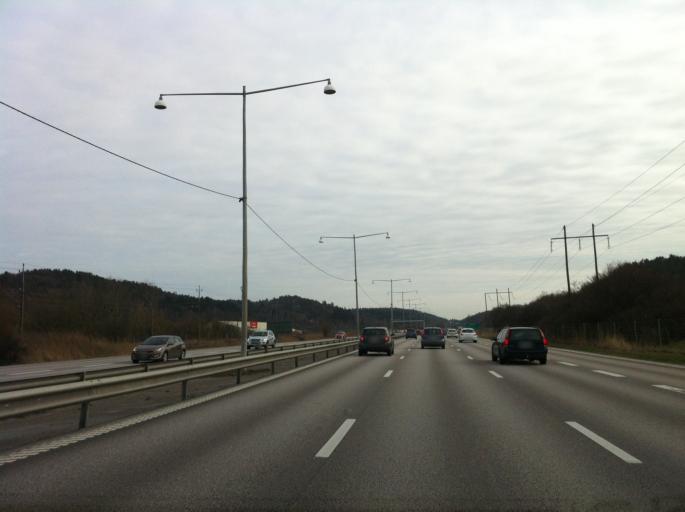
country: SE
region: Vaestra Goetaland
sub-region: Molndal
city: Moelndal
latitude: 57.6890
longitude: 12.0005
